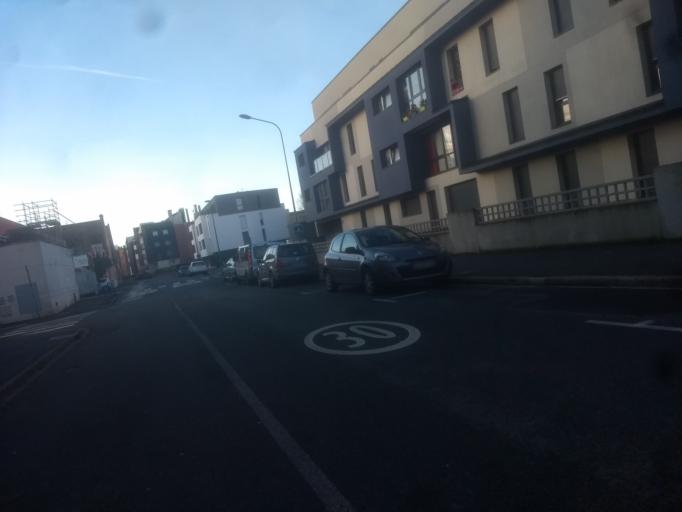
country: FR
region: Nord-Pas-de-Calais
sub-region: Departement du Pas-de-Calais
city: Arras
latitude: 50.2962
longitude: 2.7790
